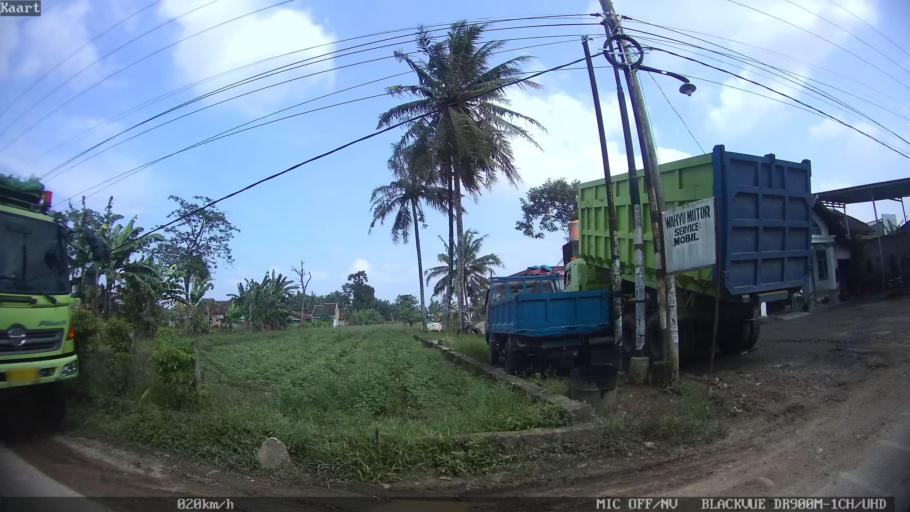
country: ID
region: Lampung
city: Kedaton
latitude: -5.3347
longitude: 105.2787
